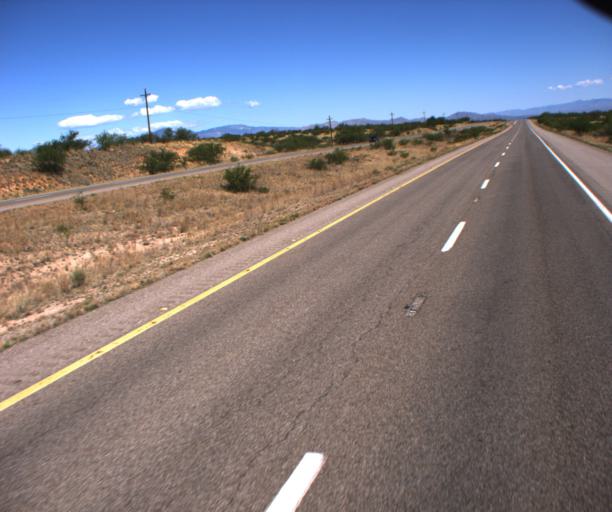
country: US
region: Arizona
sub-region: Cochise County
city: Whetstone
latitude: 31.8769
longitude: -110.3410
